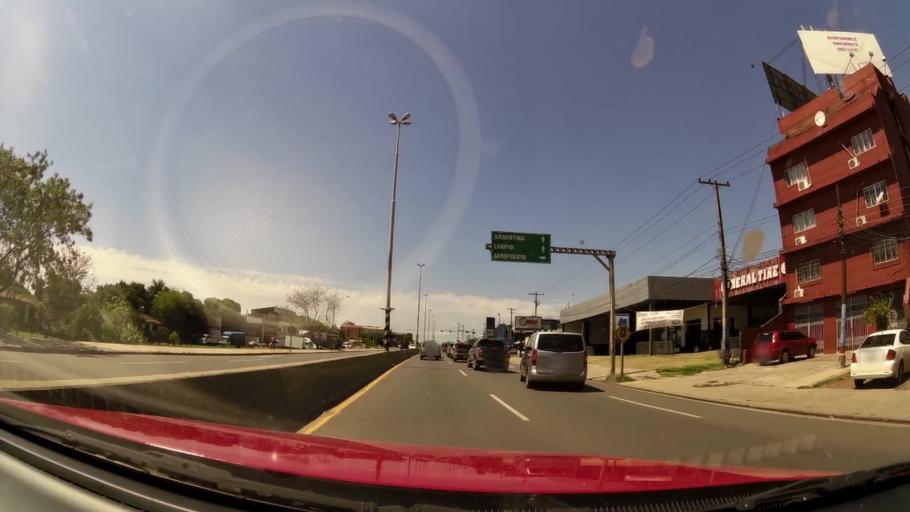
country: PY
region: Central
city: Colonia Mariano Roque Alonso
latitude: -25.2477
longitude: -57.5506
